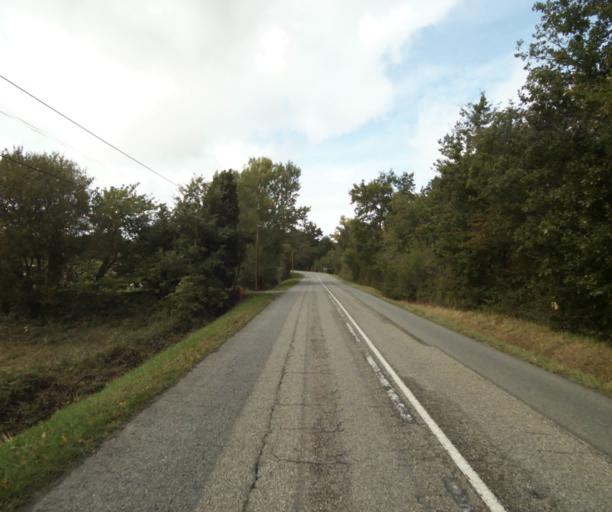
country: FR
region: Midi-Pyrenees
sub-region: Departement du Tarn-et-Garonne
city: Beaumont-de-Lomagne
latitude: 43.8645
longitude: 1.0967
